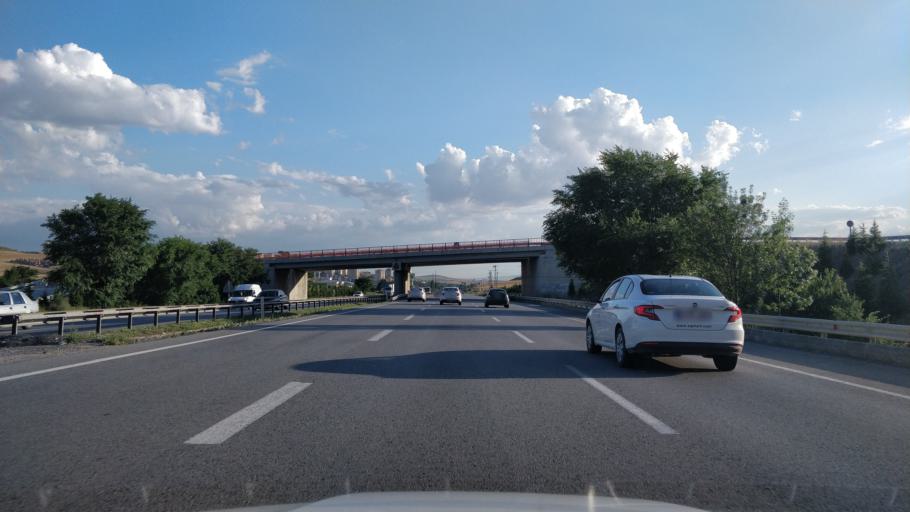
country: TR
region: Ankara
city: Etimesgut
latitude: 39.8376
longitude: 32.5869
